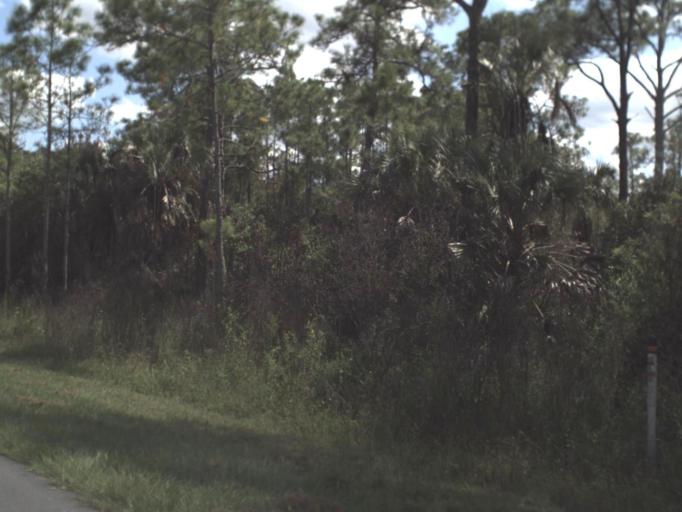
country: US
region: Florida
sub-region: Collier County
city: Marco
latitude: 25.8781
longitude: -81.2396
